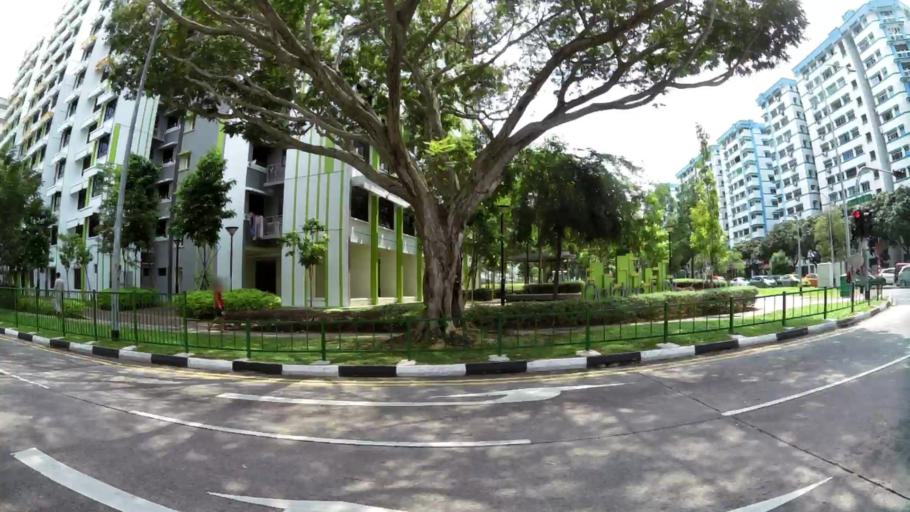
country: MY
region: Johor
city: Kampung Pasir Gudang Baru
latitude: 1.3680
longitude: 103.9596
